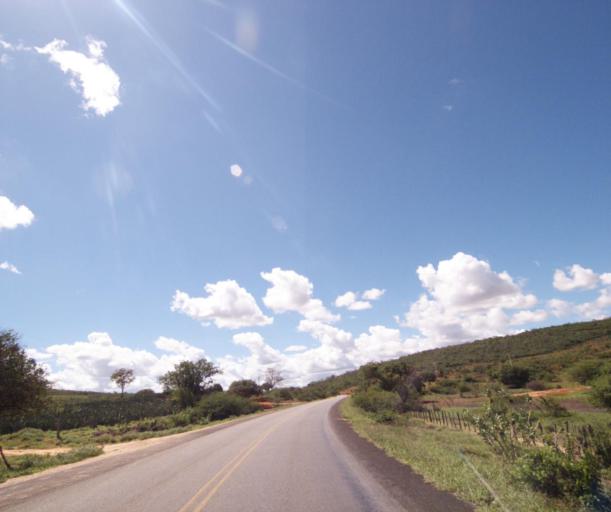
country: BR
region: Bahia
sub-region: Cacule
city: Cacule
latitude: -14.2003
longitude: -42.1345
